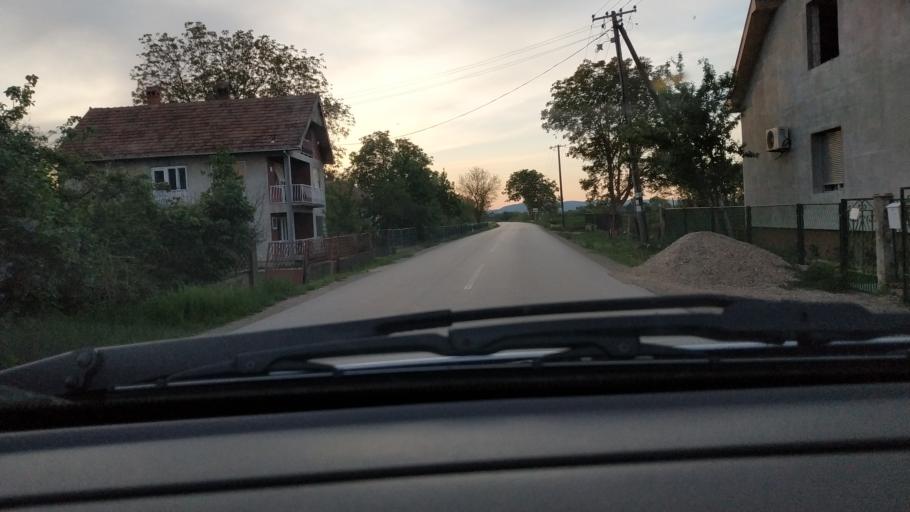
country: RS
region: Central Serbia
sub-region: Nisavski Okrug
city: Aleksinac
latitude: 43.5456
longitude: 21.6246
